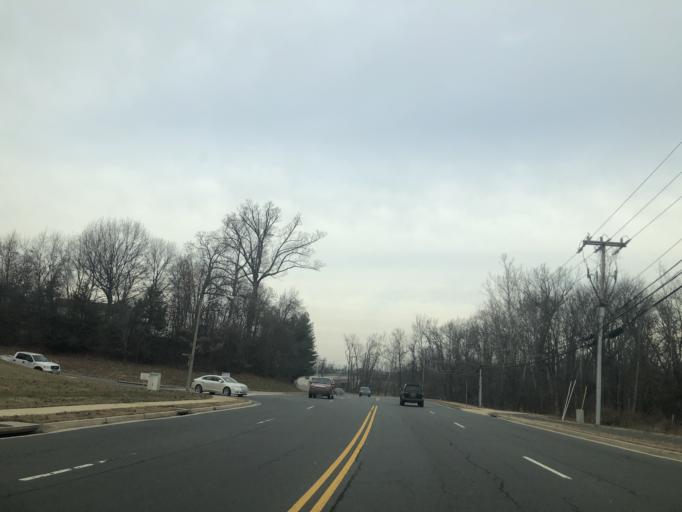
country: US
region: Virginia
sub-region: Loudoun County
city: Leesburg
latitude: 39.1016
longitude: -77.5516
